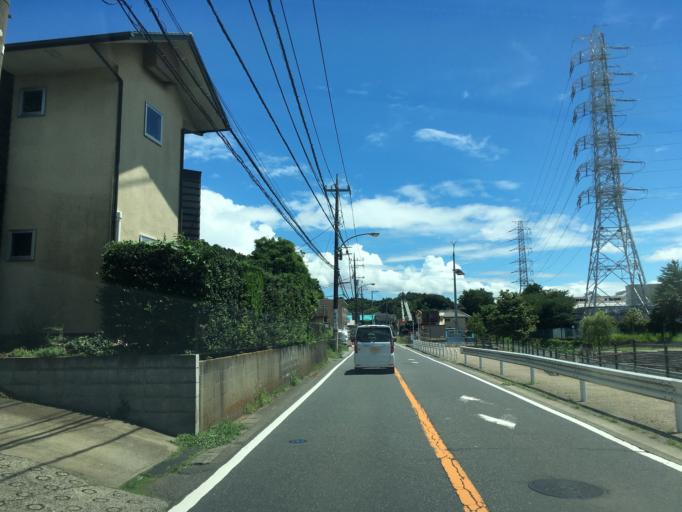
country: JP
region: Tokyo
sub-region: Machida-shi
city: Machida
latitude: 35.5455
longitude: 139.4931
